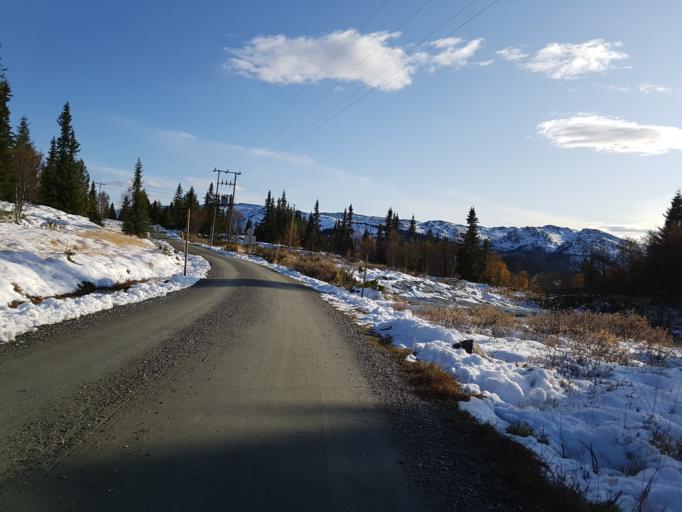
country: NO
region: Oppland
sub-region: Sel
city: Otta
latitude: 61.8171
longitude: 9.6775
